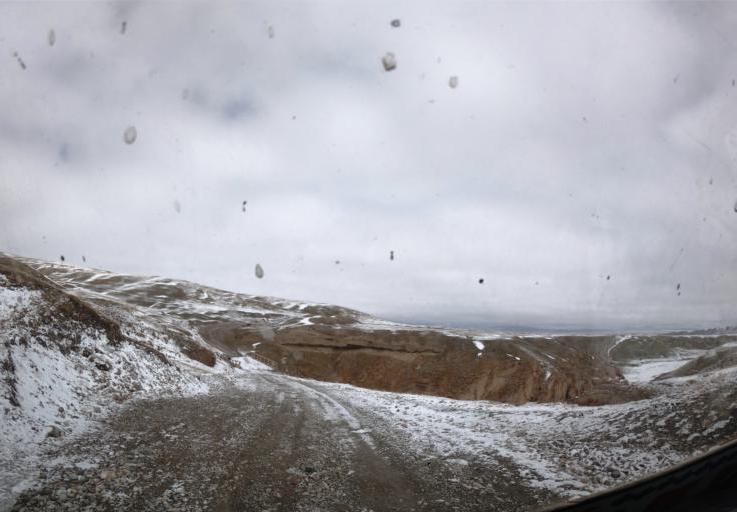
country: KG
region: Naryn
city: At-Bashi
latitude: 40.8074
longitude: 76.2640
